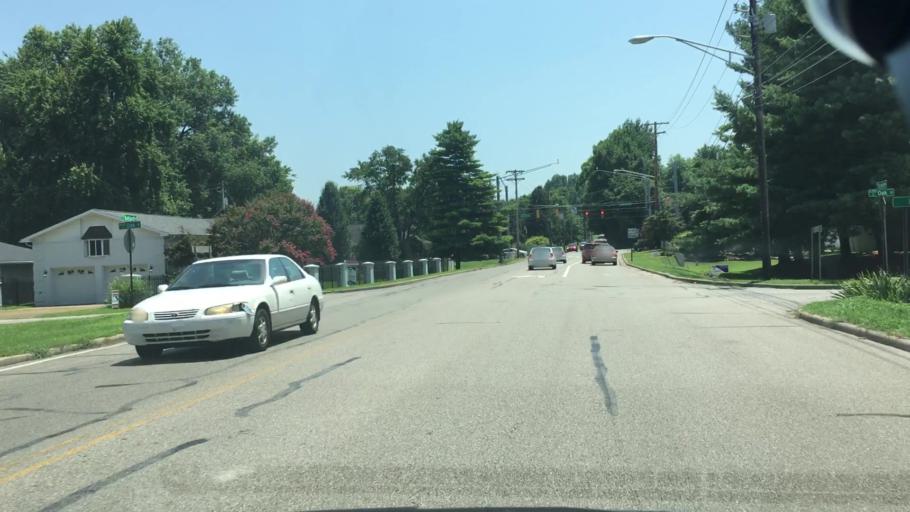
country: US
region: Indiana
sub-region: Vanderburgh County
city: Melody Hill
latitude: 37.9705
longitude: -87.4744
